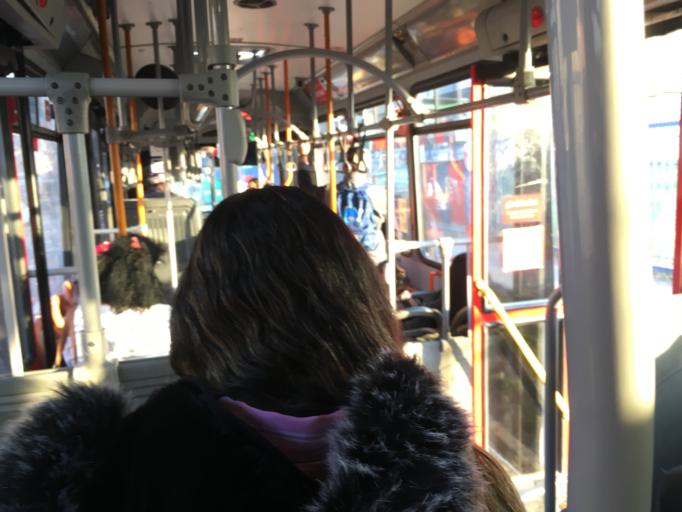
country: CL
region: Santiago Metropolitan
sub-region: Provincia de Santiago
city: Lo Prado
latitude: -33.3759
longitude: -70.7259
